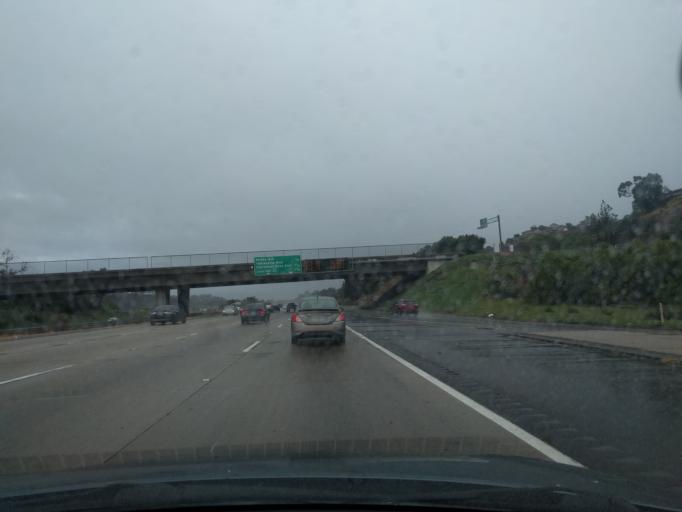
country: US
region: California
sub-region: San Diego County
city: La Mesa
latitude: 32.8096
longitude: -117.1137
